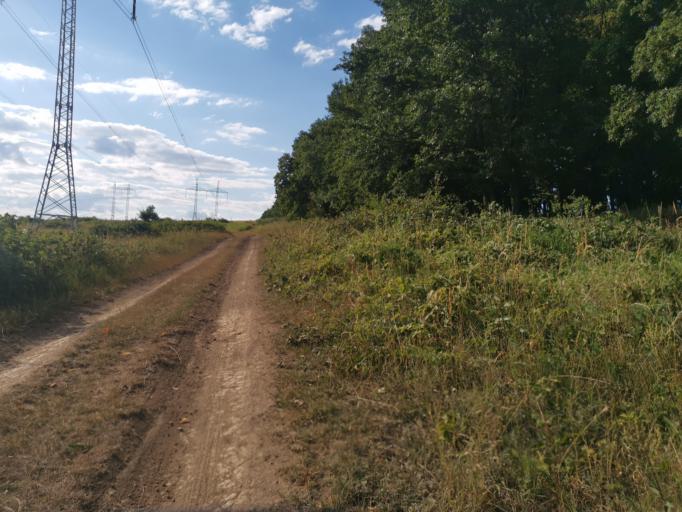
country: CZ
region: South Moravian
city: Sudomerice
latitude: 48.8094
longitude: 17.2908
